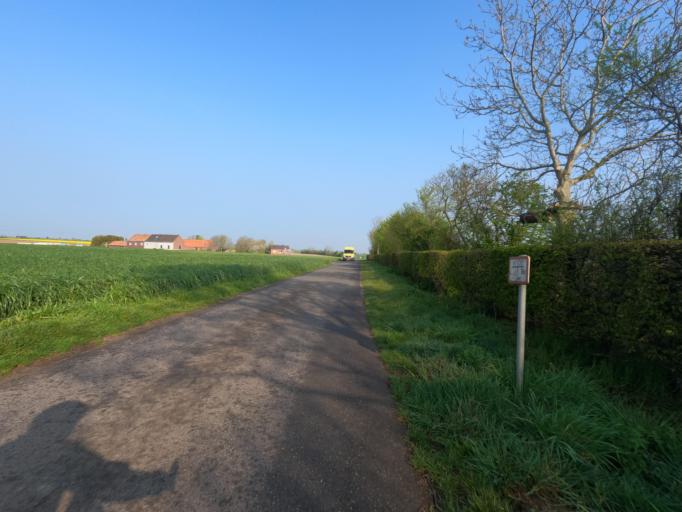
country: DE
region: North Rhine-Westphalia
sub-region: Regierungsbezirk Koln
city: Heinsberg
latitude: 51.0337
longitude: 6.1294
